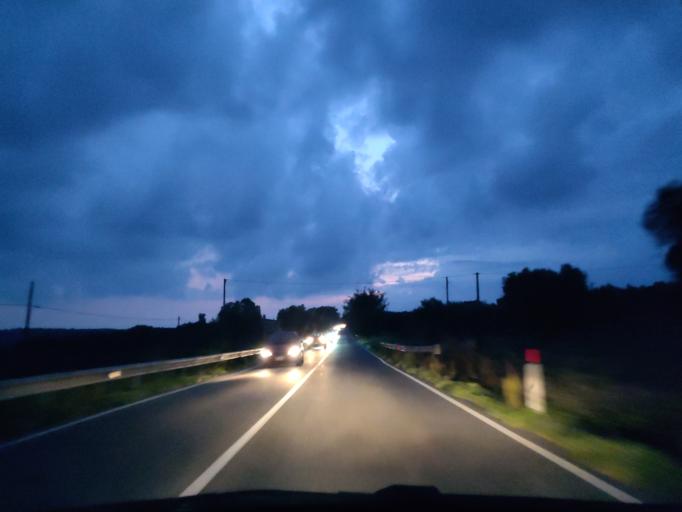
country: IT
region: Latium
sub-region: Provincia di Viterbo
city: Monte Romano
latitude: 42.2645
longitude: 11.8739
